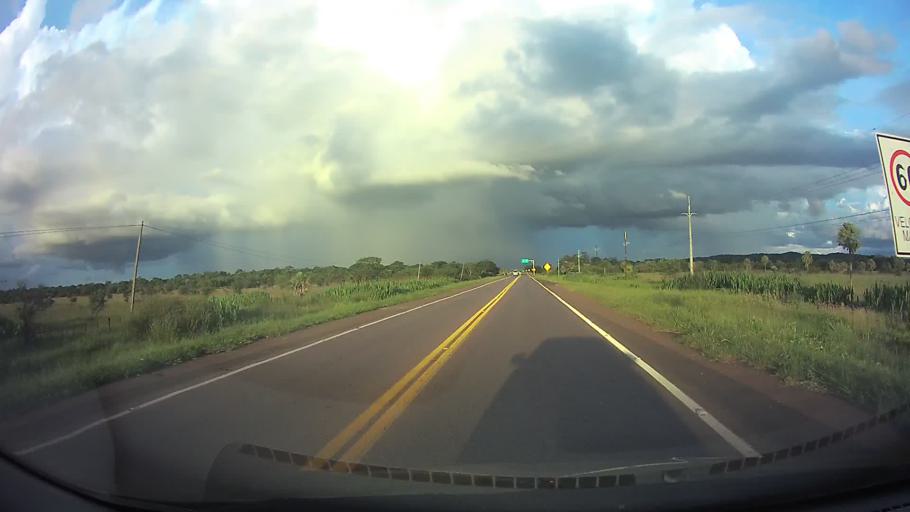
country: PY
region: Paraguari
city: Carapegua
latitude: -25.7516
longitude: -57.2220
